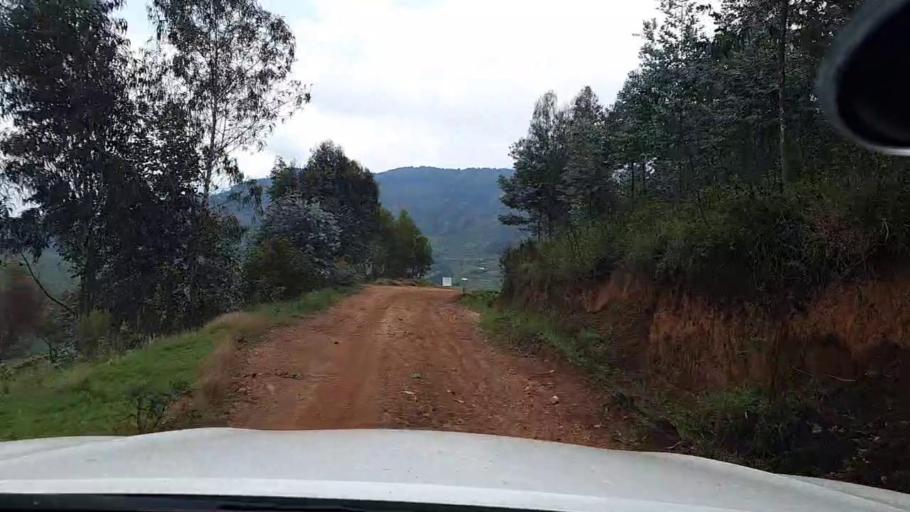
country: RW
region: Western Province
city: Kibuye
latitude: -2.1614
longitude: 29.4522
